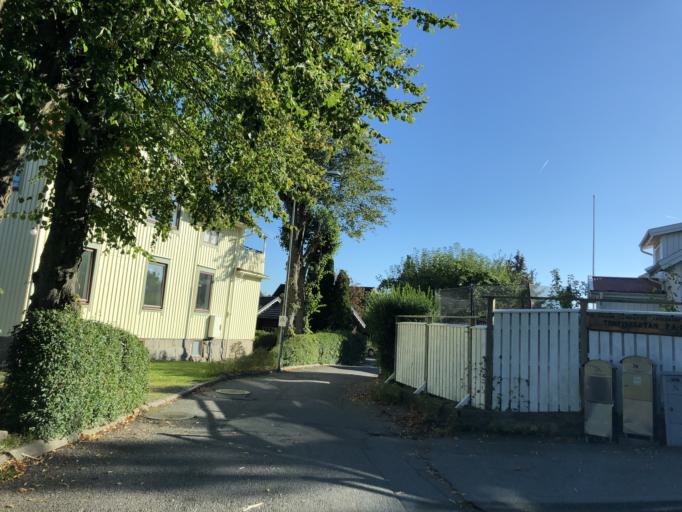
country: SE
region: Vaestra Goetaland
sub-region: Goteborg
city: Majorna
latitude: 57.6503
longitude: 11.8641
